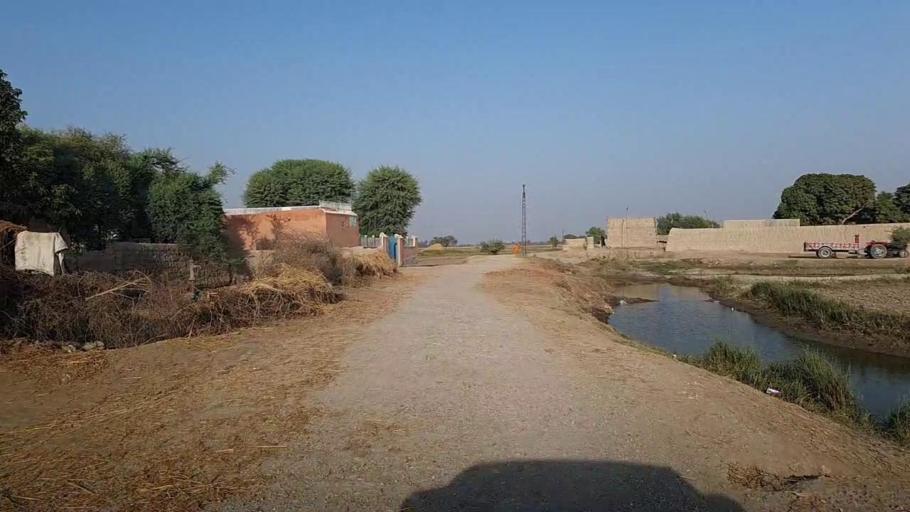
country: PK
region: Sindh
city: Kashmor
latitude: 28.4235
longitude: 69.4247
